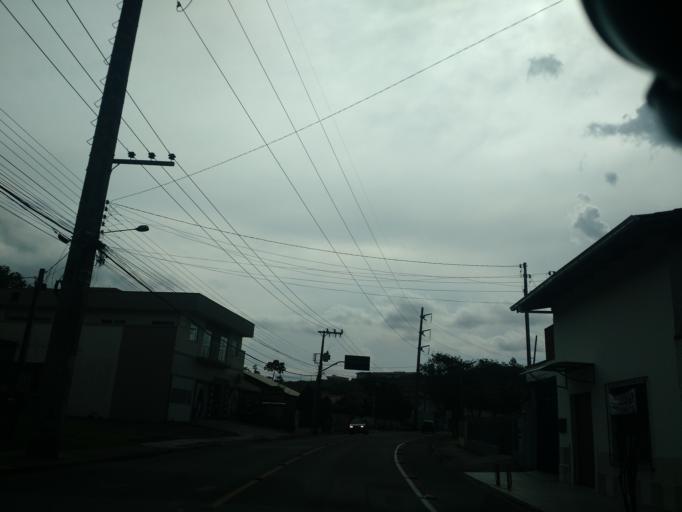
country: BR
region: Santa Catarina
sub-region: Jaragua Do Sul
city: Jaragua do Sul
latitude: -26.4800
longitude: -49.1059
